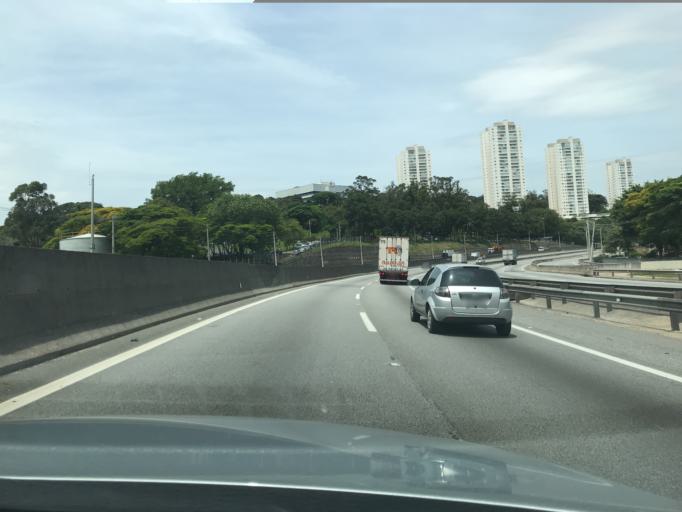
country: BR
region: Sao Paulo
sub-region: Osasco
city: Osasco
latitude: -23.4946
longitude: -46.7564
